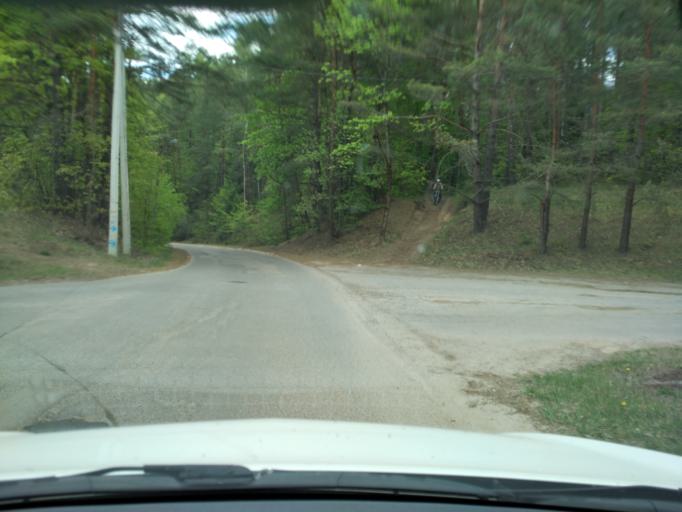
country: LT
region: Vilnius County
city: Rasos
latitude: 54.6957
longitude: 25.3263
